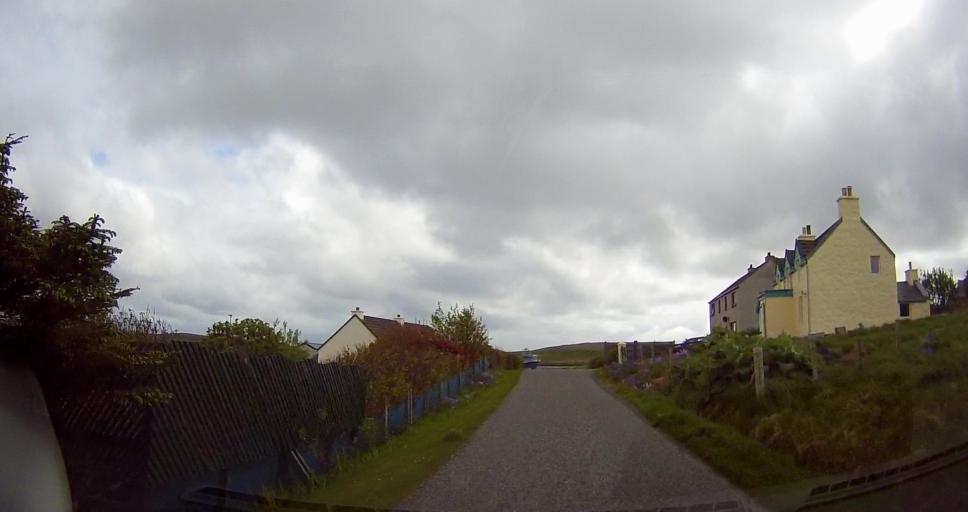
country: GB
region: Scotland
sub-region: Shetland Islands
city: Sandwick
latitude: 60.2248
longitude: -1.5700
